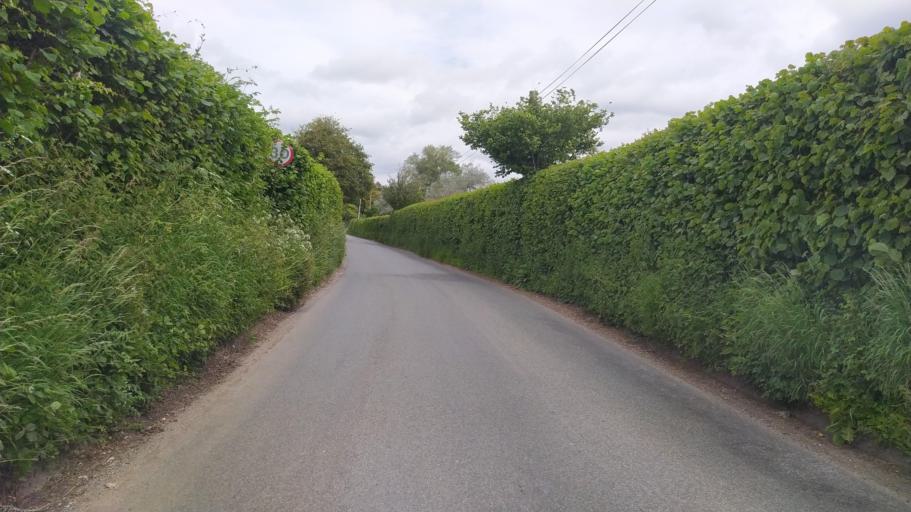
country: GB
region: England
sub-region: Dorset
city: Manston
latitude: 50.8995
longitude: -2.2565
